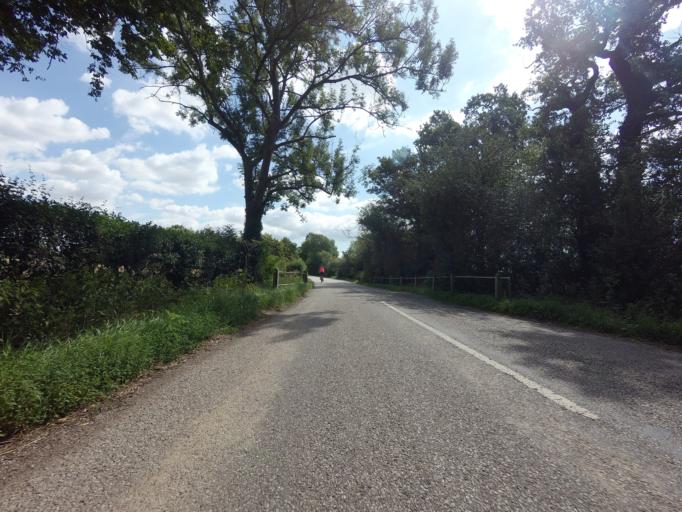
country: GB
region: England
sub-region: Kent
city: Tenterden
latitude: 51.0739
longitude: 0.7278
